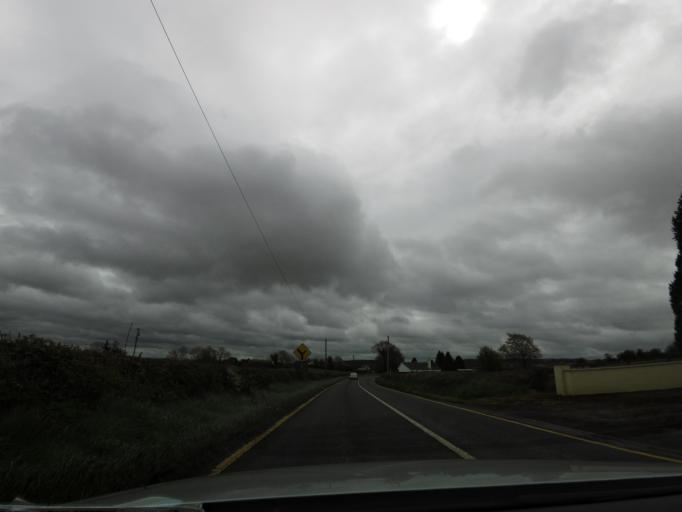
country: IE
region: Leinster
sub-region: Kilkenny
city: Ballyragget
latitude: 52.7221
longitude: -7.3474
